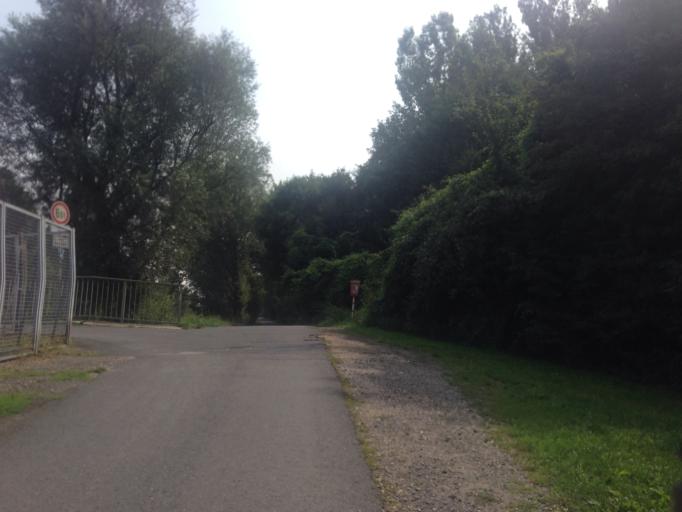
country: DE
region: Hesse
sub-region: Regierungsbezirk Darmstadt
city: Eschborn
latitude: 50.1133
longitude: 8.5901
